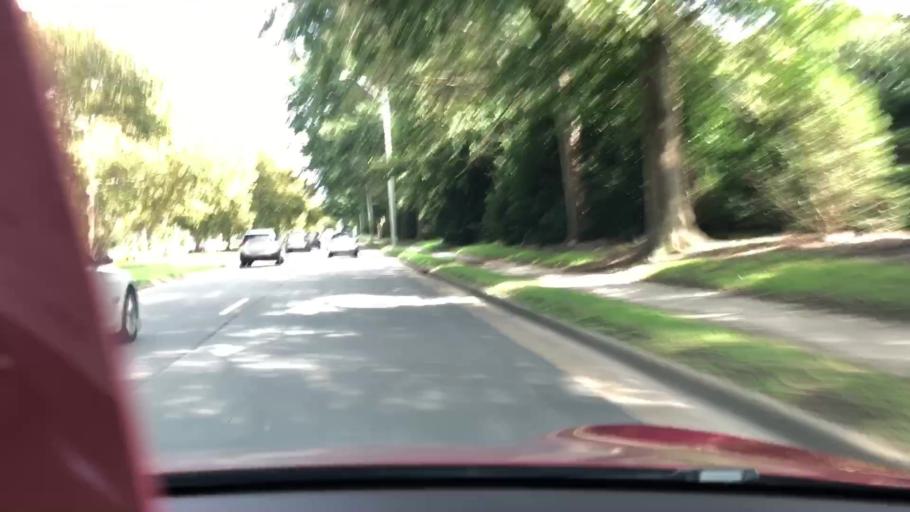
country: US
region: Virginia
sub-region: City of Virginia Beach
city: Virginia Beach
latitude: 36.8932
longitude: -76.0575
